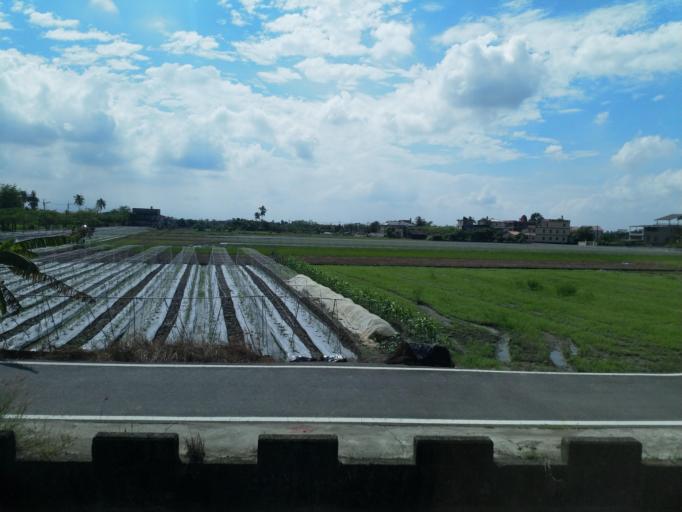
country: TW
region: Taiwan
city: Yujing
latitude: 22.9055
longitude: 120.5296
